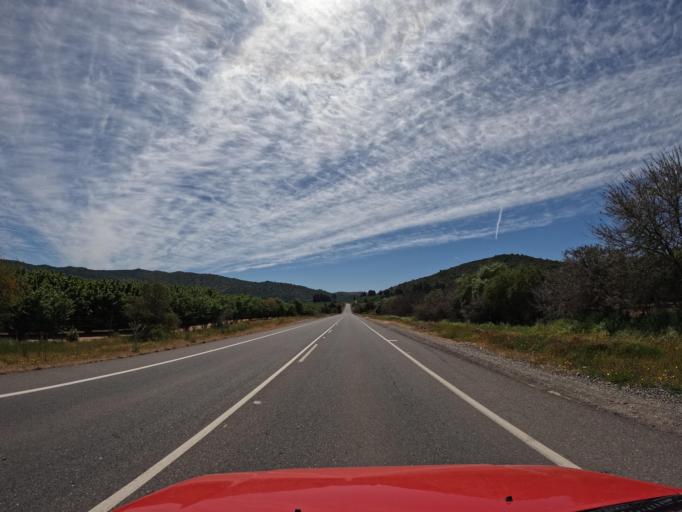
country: CL
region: Maule
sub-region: Provincia de Talca
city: Talca
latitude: -35.2650
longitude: -71.5413
